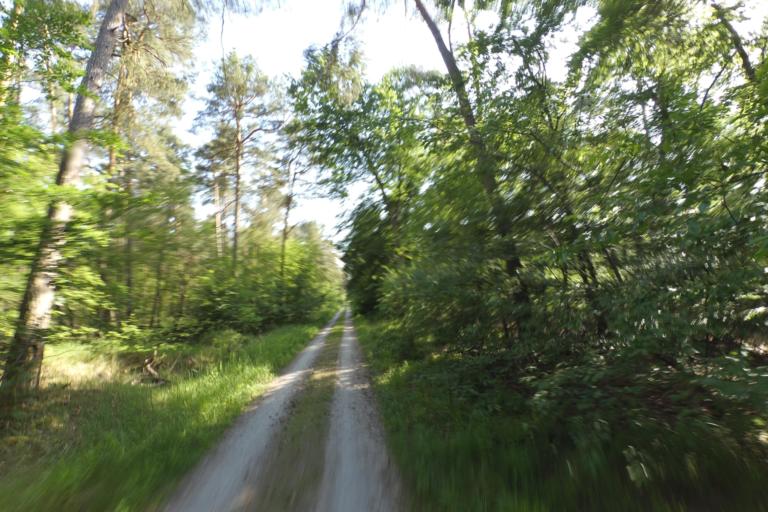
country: DE
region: Hesse
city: Viernheim
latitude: 49.5768
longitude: 8.5370
